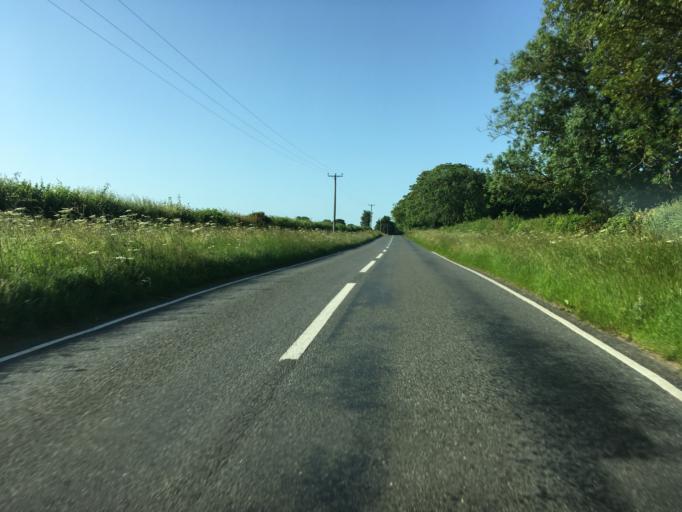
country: GB
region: England
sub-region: Oxfordshire
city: Charlbury
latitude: 51.8989
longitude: -1.4675
